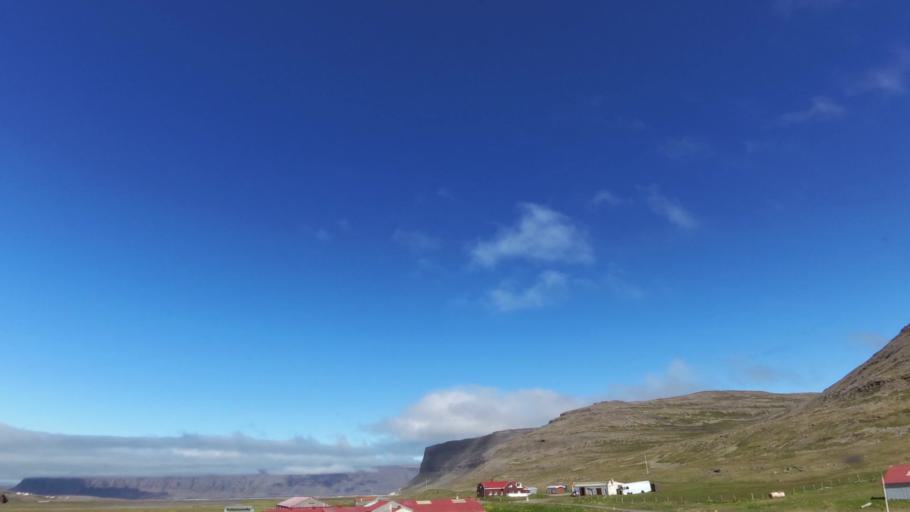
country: IS
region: West
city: Olafsvik
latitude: 65.5623
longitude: -24.1578
